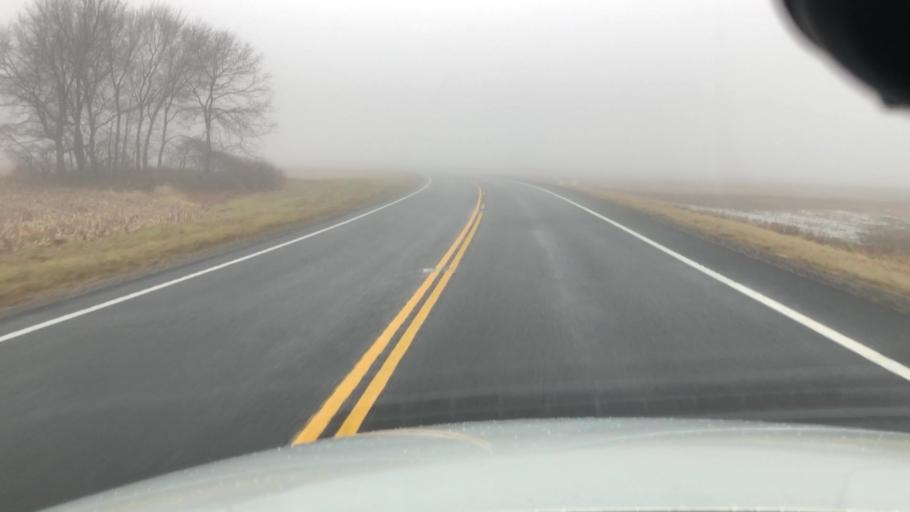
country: US
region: Ohio
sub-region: Logan County
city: Russells Point
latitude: 40.5777
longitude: -83.8508
